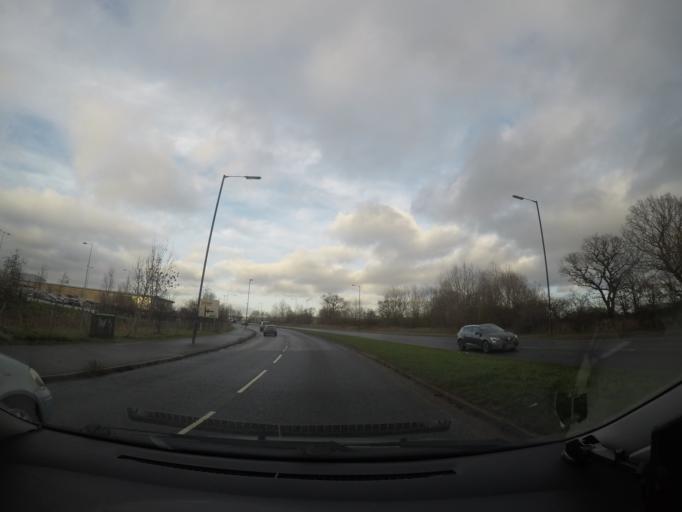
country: GB
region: England
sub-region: City of York
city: Huntington
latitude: 53.9832
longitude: -1.0446
